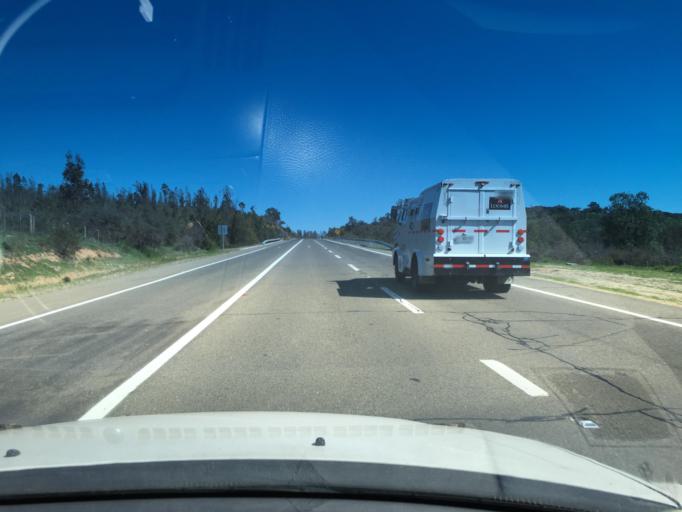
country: CL
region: Valparaiso
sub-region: San Antonio Province
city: El Tabo
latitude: -33.4038
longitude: -71.5019
